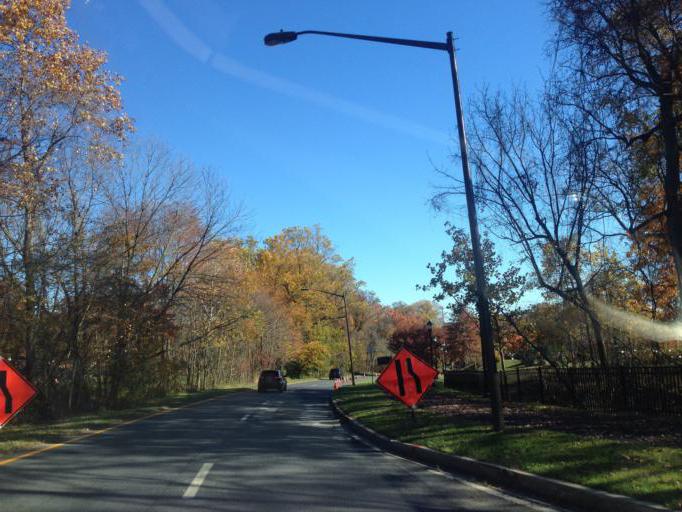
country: US
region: Maryland
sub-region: Howard County
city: Riverside
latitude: 39.2162
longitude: -76.8799
